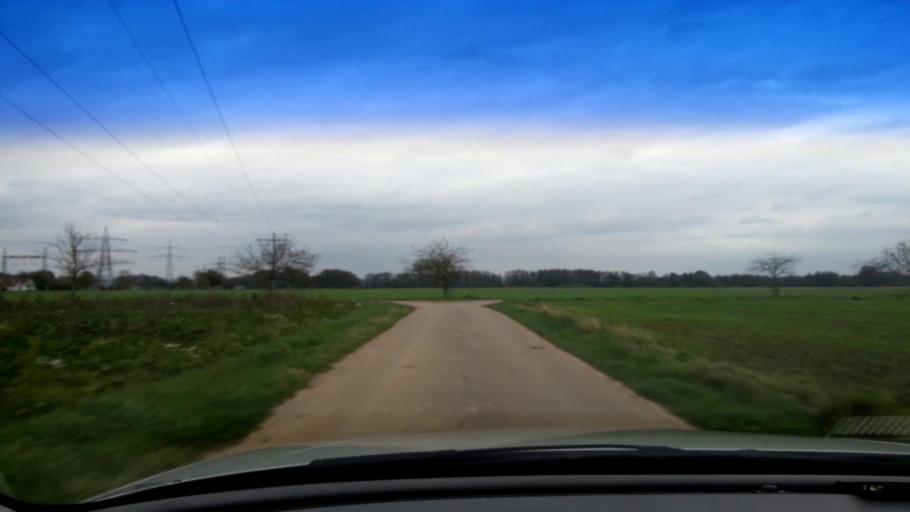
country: DE
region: Bavaria
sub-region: Upper Franconia
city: Bischberg
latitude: 49.9266
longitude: 10.8310
